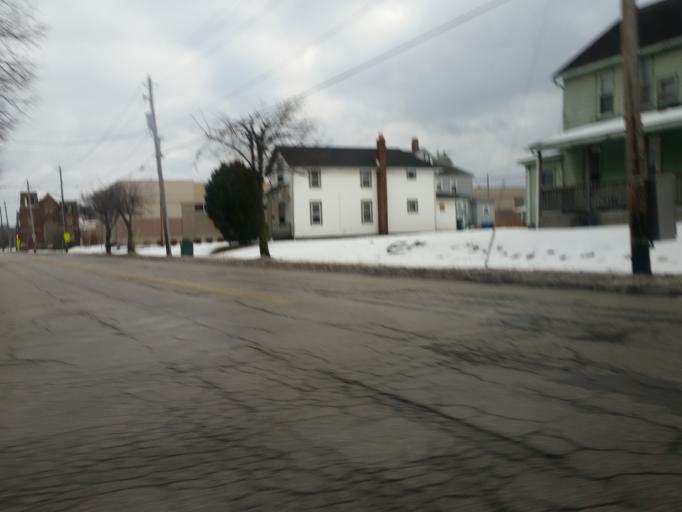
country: US
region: Ohio
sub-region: Summit County
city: Barberton
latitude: 41.0177
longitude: -81.6096
